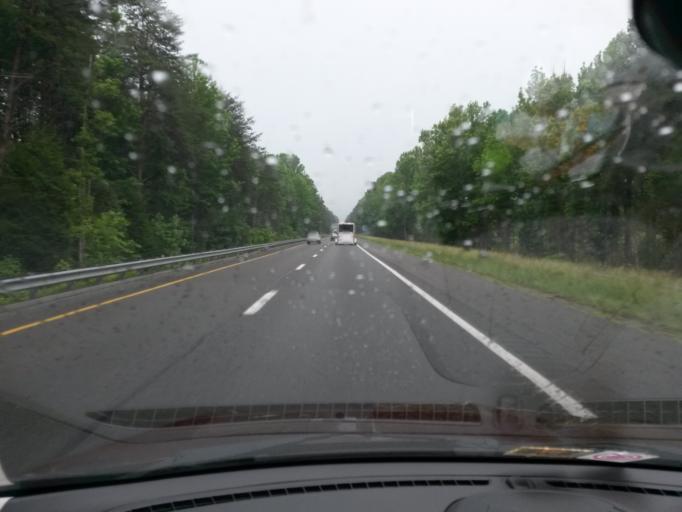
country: US
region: Virginia
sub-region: Louisa County
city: Louisa
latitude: 37.8553
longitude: -77.9948
